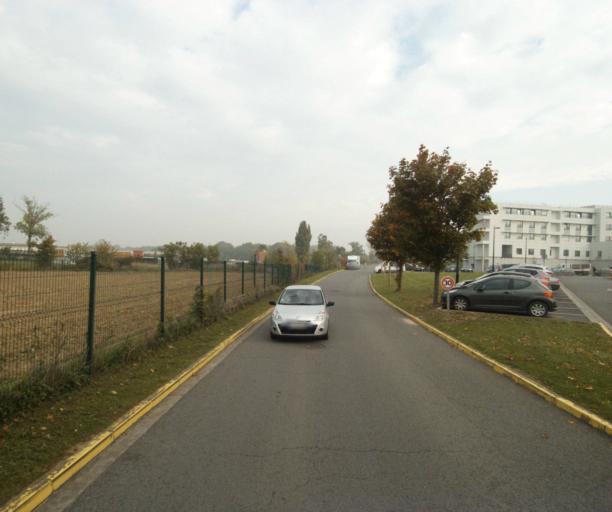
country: FR
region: Nord-Pas-de-Calais
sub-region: Departement du Nord
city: Seclin
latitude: 50.5457
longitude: 3.0156
